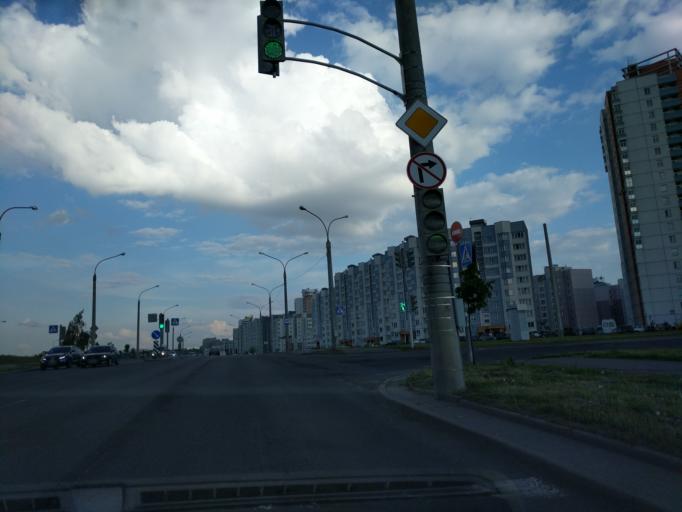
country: BY
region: Minsk
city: Zhdanovichy
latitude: 53.9350
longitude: 27.4336
